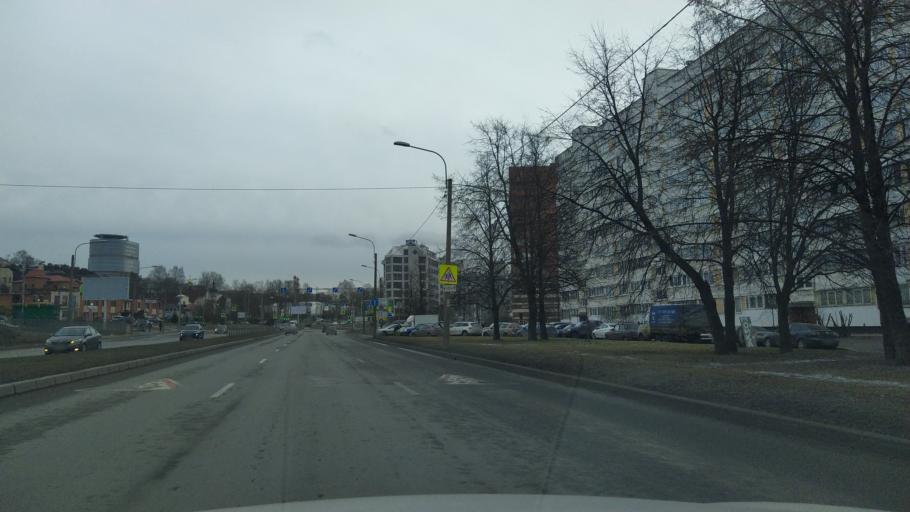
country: RU
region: St.-Petersburg
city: Kolomyagi
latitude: 60.0157
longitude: 30.2903
